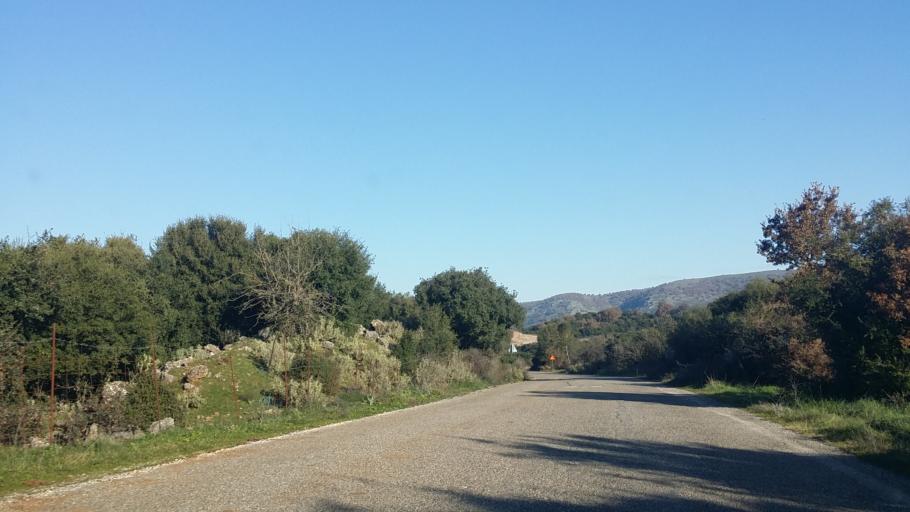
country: GR
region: West Greece
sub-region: Nomos Aitolias kai Akarnanias
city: Katouna
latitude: 38.7688
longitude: 21.1337
